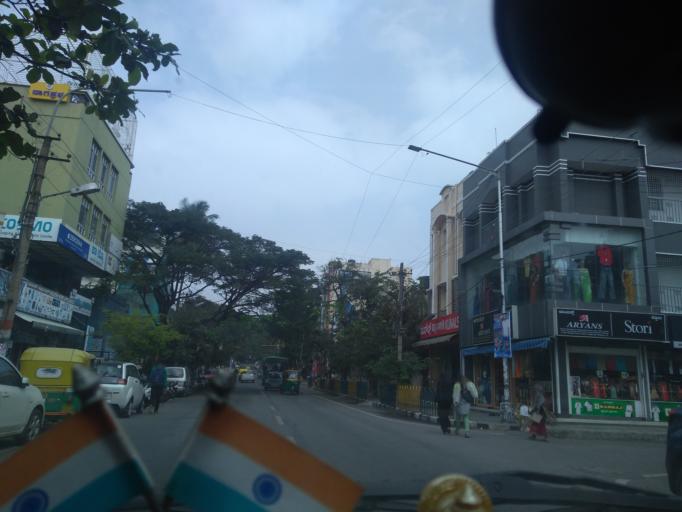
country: IN
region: Karnataka
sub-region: Bangalore Urban
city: Bangalore
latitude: 13.0029
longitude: 77.5502
